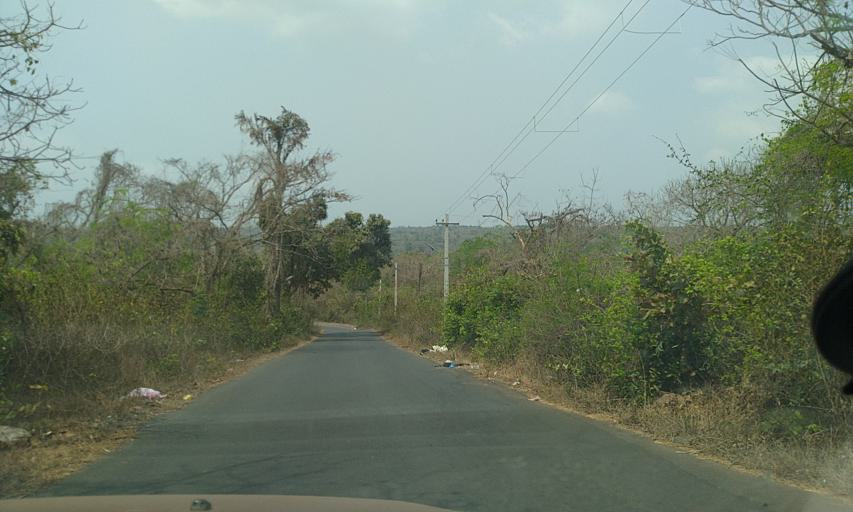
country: IN
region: Goa
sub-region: North Goa
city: Goa Velha
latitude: 15.4810
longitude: 73.8940
